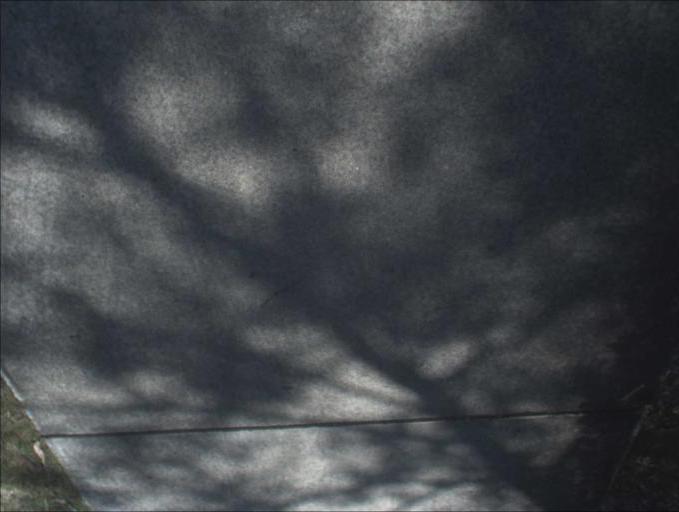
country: AU
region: Queensland
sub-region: Logan
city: Waterford West
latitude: -27.7105
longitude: 153.1565
